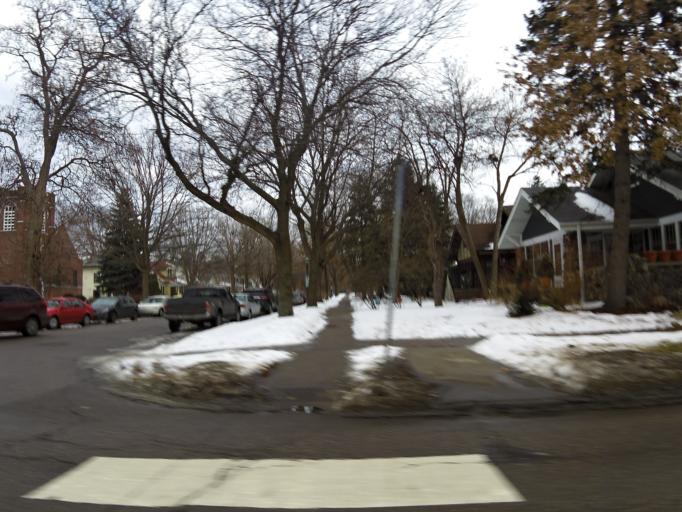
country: US
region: Minnesota
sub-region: Ramsey County
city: Falcon Heights
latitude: 44.9378
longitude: -93.1670
